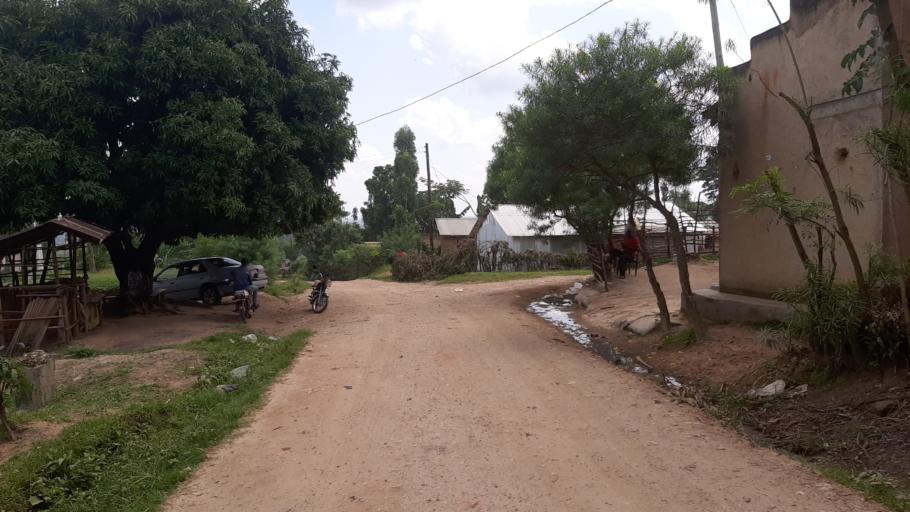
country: UG
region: Eastern Region
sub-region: Mbale District
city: Mbale
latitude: 1.0620
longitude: 34.2052
